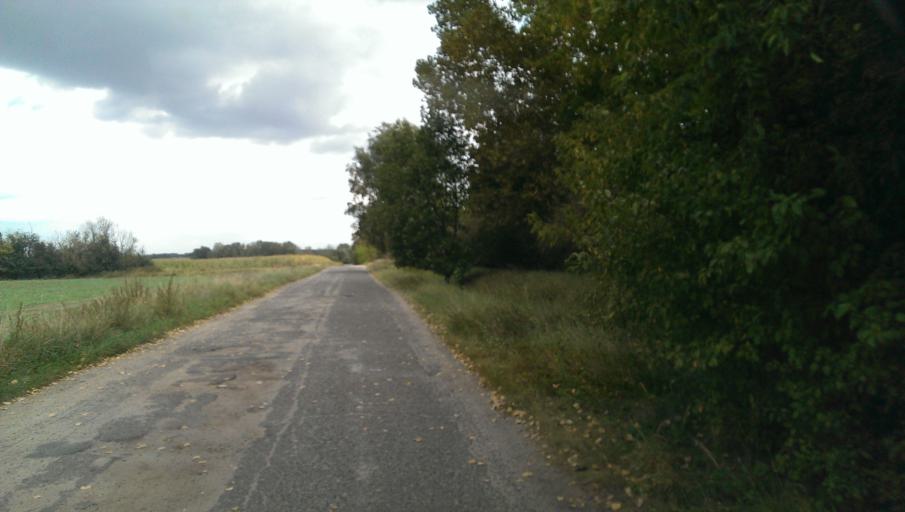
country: DE
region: Brandenburg
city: Rangsdorf
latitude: 52.2906
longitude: 13.4738
